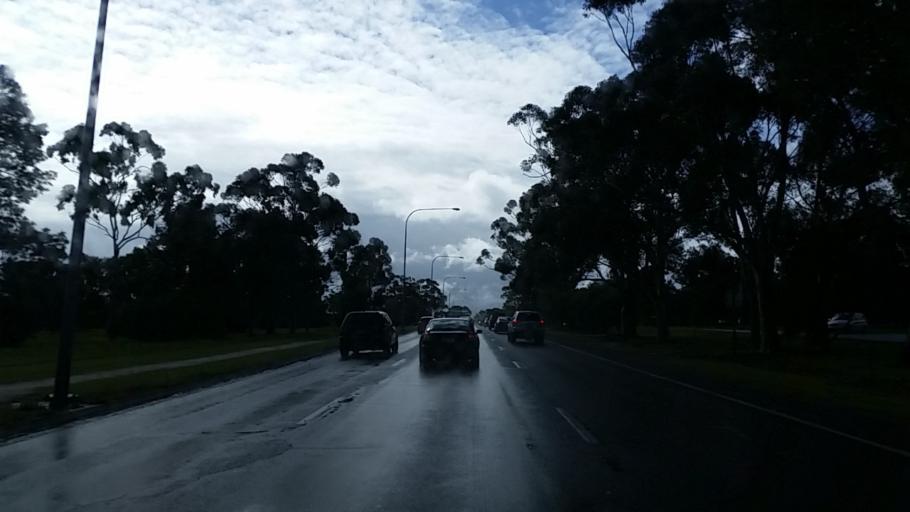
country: AU
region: South Australia
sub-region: Salisbury
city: Elizabeth
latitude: -34.7400
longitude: 138.6759
